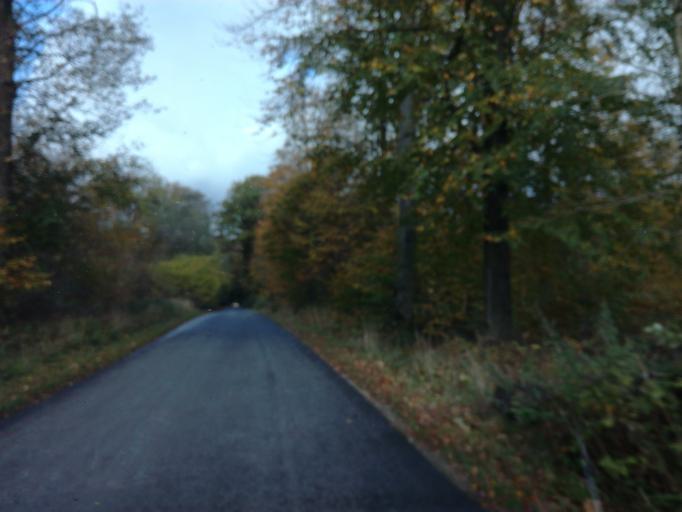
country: DK
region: South Denmark
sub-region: Vejle Kommune
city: Borkop
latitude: 55.6807
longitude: 9.6018
